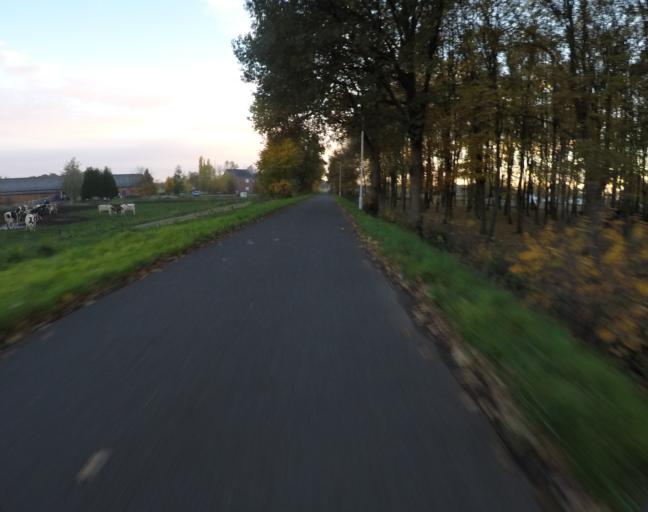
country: BE
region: Flanders
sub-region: Provincie Antwerpen
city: Herentals
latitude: 51.1544
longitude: 4.8202
